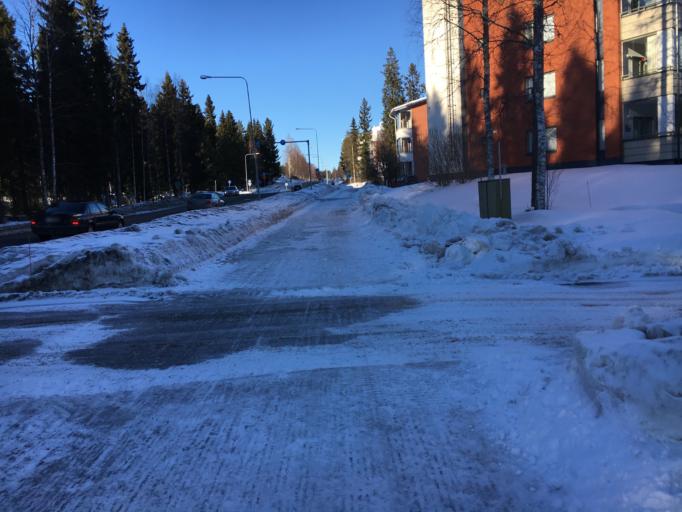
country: FI
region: Kainuu
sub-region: Kajaani
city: Kajaani
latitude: 64.2288
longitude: 27.7525
